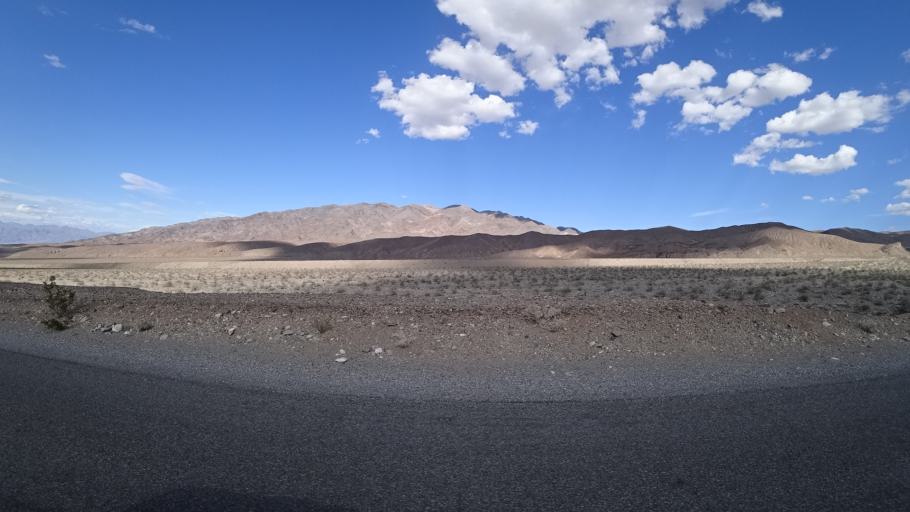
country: US
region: Nevada
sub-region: Nye County
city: Beatty
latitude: 36.4879
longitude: -117.2225
